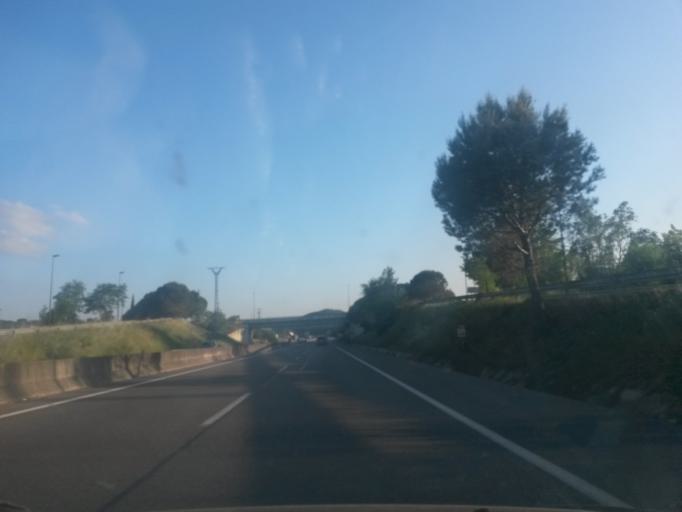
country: ES
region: Catalonia
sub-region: Provincia de Girona
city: Cornella del Terri
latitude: 42.0742
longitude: 2.8159
